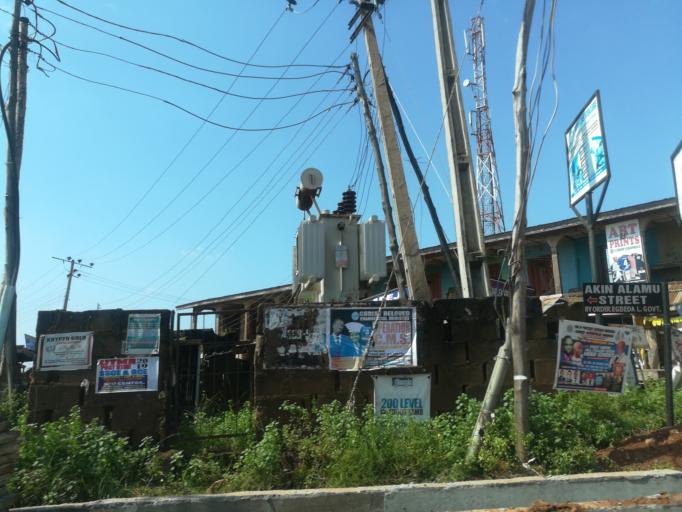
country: NG
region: Oyo
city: Ibadan
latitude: 7.4168
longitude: 3.9773
